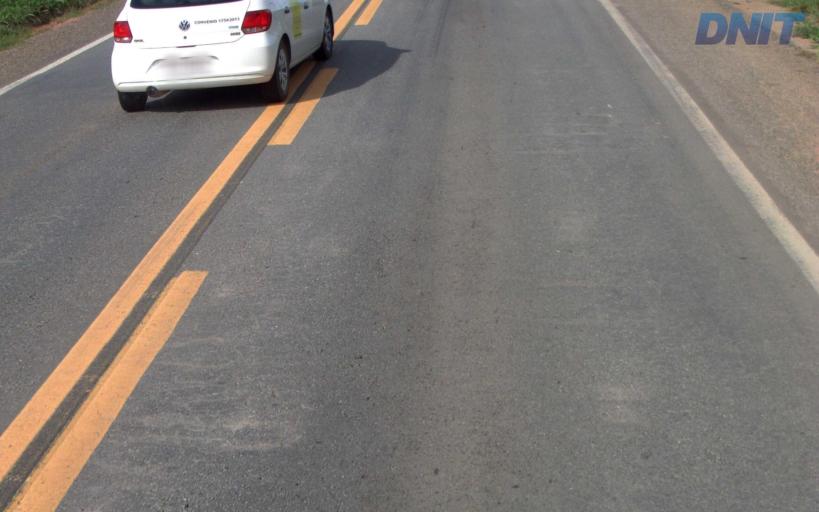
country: BR
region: Minas Gerais
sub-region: Belo Oriente
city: Belo Oriente
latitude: -19.1956
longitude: -42.2810
